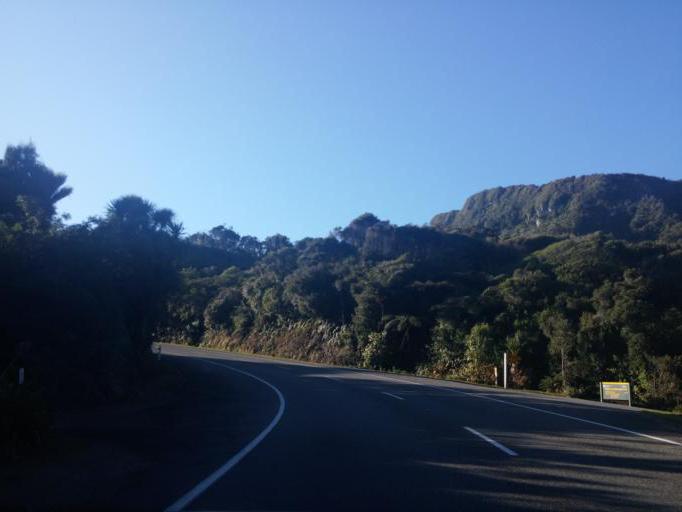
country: NZ
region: West Coast
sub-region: Grey District
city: Greymouth
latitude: -42.1002
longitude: 171.3420
